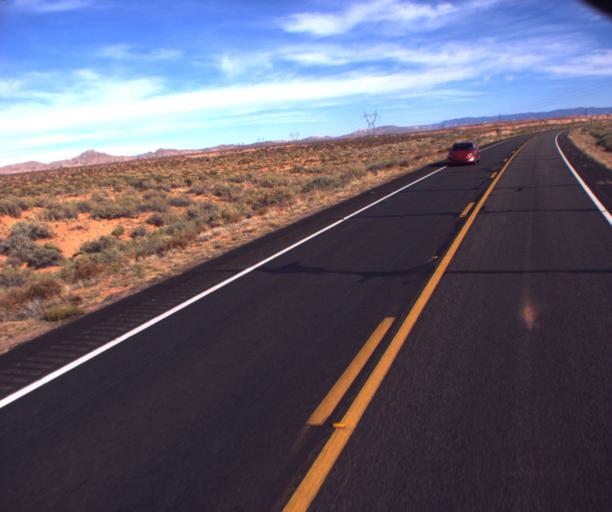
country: US
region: Arizona
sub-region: Apache County
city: Many Farms
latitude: 36.9406
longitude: -109.6434
